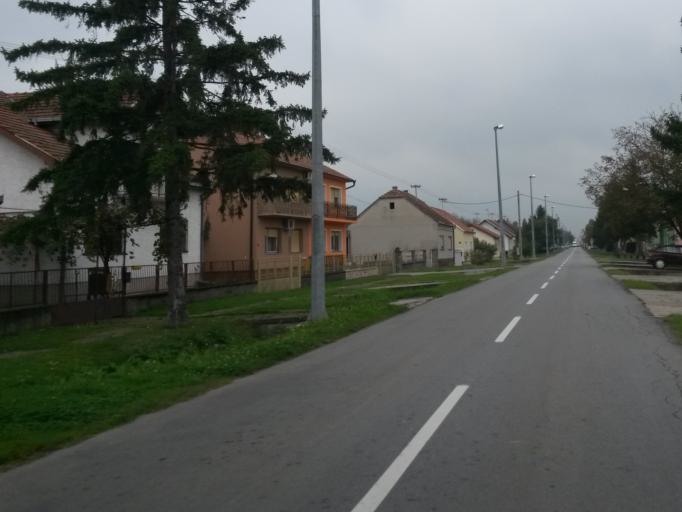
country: HR
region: Osjecko-Baranjska
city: Visnjevac
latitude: 45.5269
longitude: 18.6267
